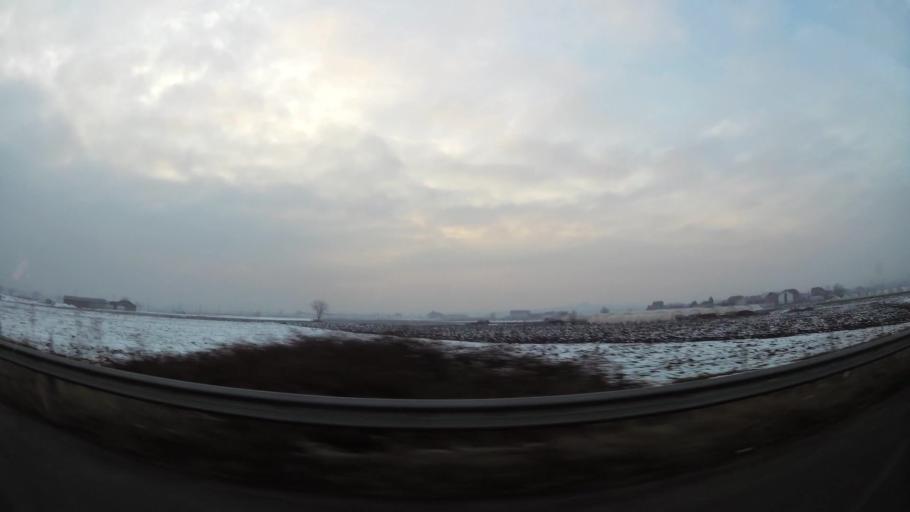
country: MK
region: Aracinovo
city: Arachinovo
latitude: 42.0091
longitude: 21.5348
